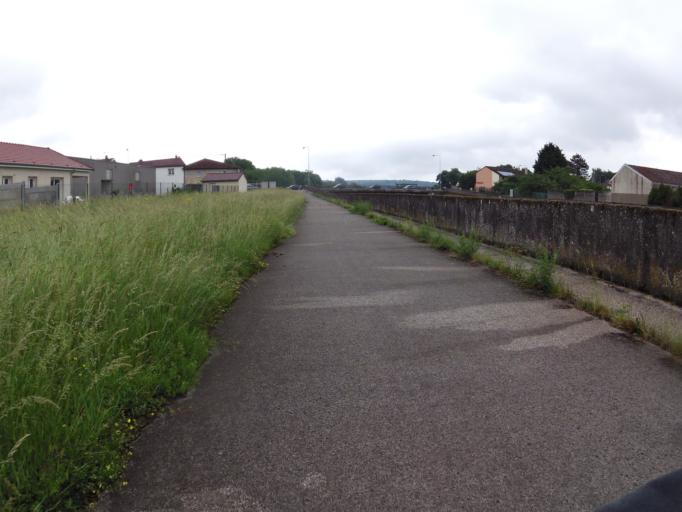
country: FR
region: Champagne-Ardenne
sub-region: Departement de la Haute-Marne
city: Saint-Dizier
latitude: 48.6271
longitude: 4.9581
